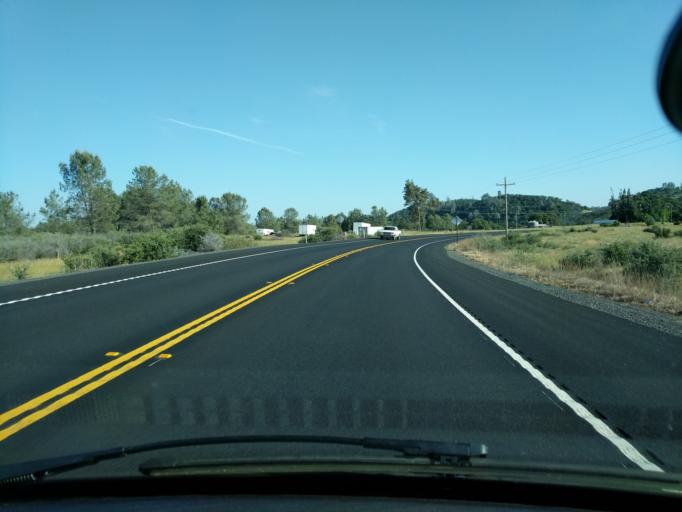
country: US
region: California
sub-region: Calaveras County
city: Copperopolis
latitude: 38.0196
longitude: -120.6428
